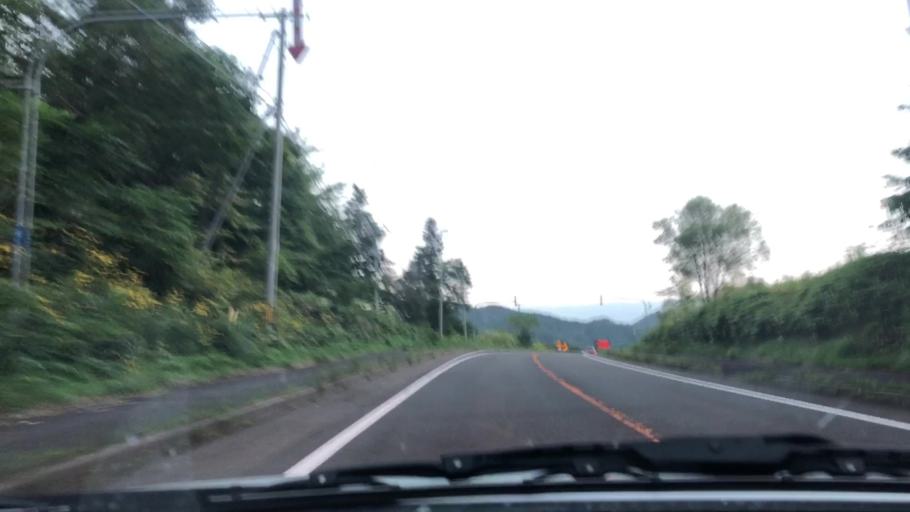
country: JP
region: Hokkaido
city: Iwamizawa
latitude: 42.9287
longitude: 142.0358
